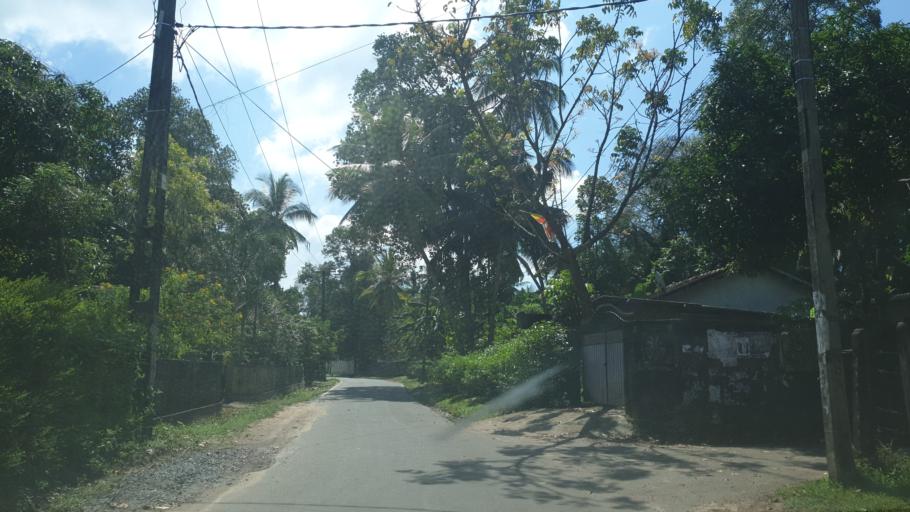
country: LK
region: Western
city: Panadura
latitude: 6.6783
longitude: 79.9300
